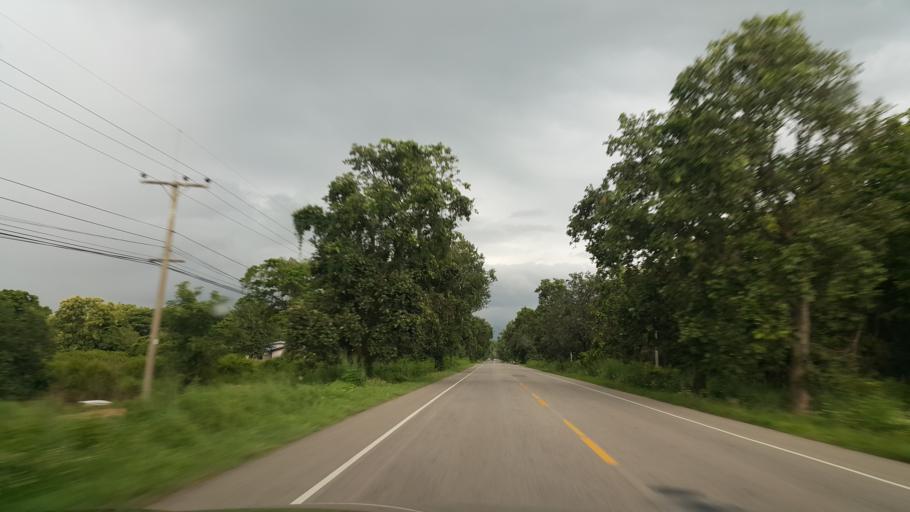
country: TH
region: Phayao
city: Dok Kham Tai
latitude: 19.2130
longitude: 100.0387
